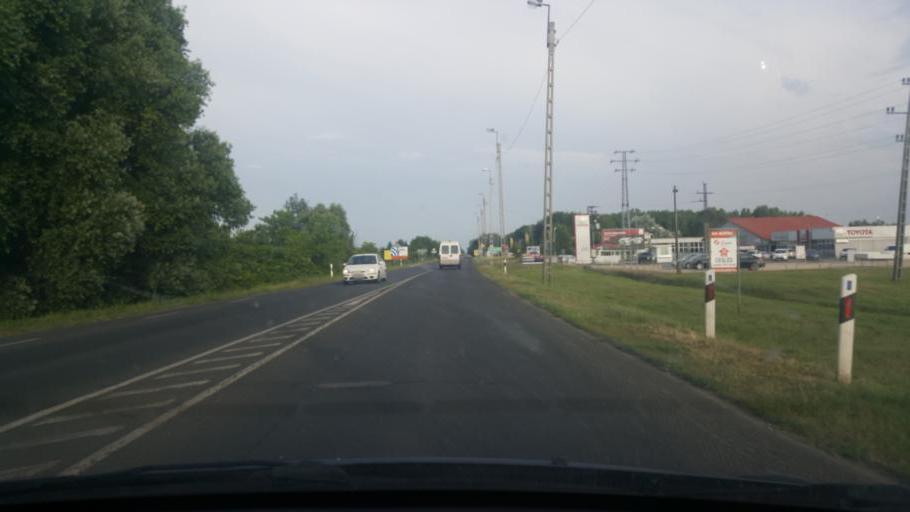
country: HU
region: Pest
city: Monor
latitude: 47.3436
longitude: 19.4226
